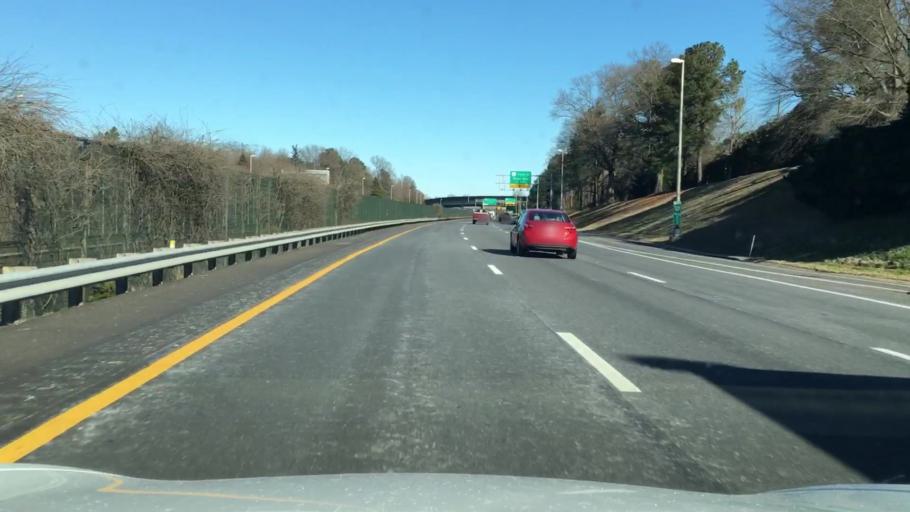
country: US
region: Virginia
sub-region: City of Richmond
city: Richmond
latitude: 37.5485
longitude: -77.4912
